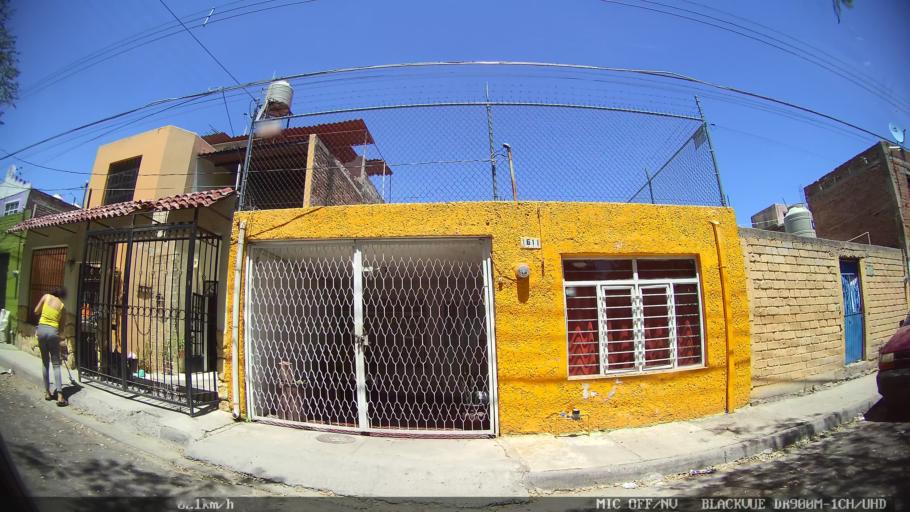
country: MX
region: Jalisco
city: Tlaquepaque
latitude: 20.6848
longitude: -103.2817
